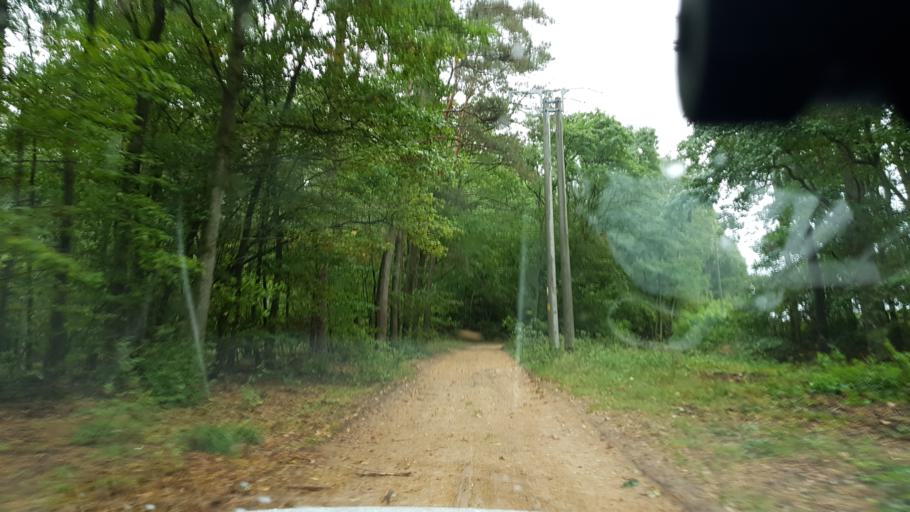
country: PL
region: West Pomeranian Voivodeship
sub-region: Powiat goleniowski
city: Przybiernow
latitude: 53.7483
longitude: 14.7565
